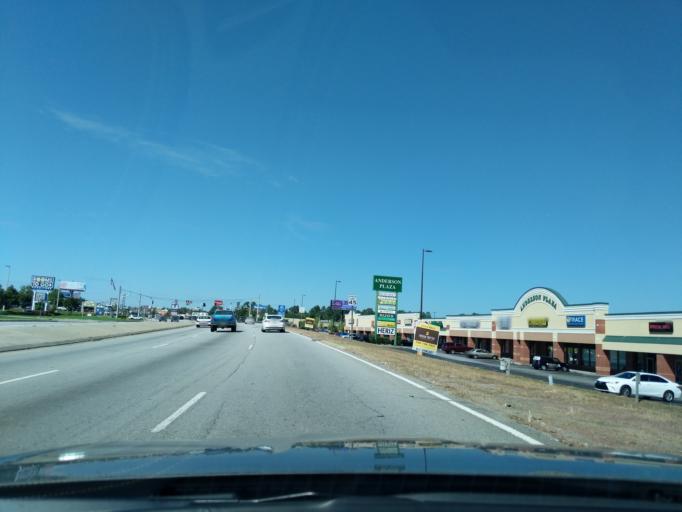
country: US
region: Georgia
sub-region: Columbia County
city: Martinez
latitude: 33.5015
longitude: -82.0874
